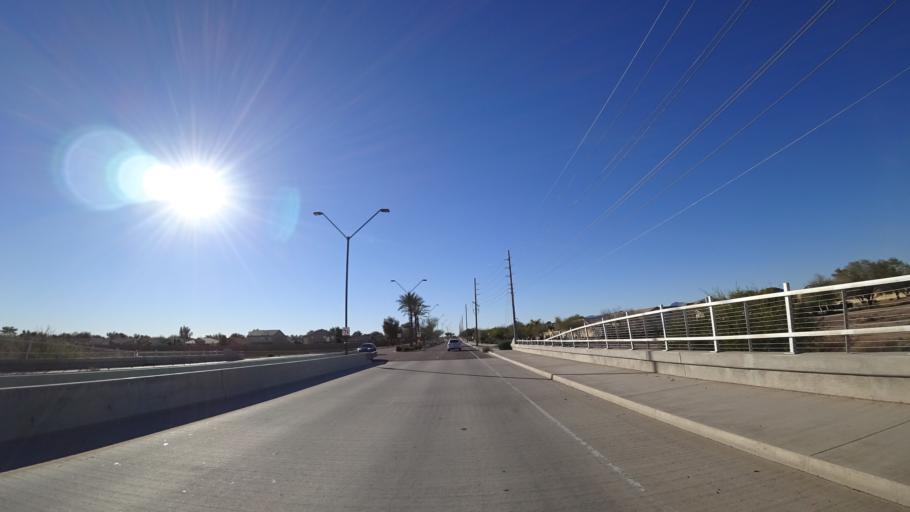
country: US
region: Arizona
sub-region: Maricopa County
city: Goodyear
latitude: 33.4500
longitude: -112.3823
